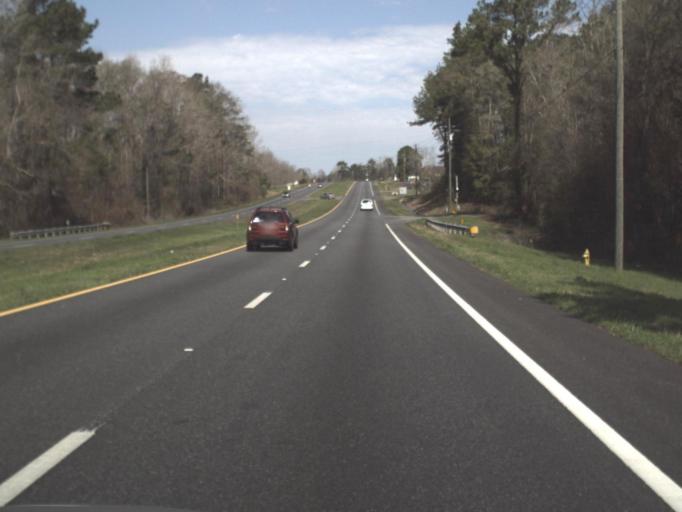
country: US
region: Florida
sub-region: Gadsden County
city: Havana
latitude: 30.5828
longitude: -84.4006
